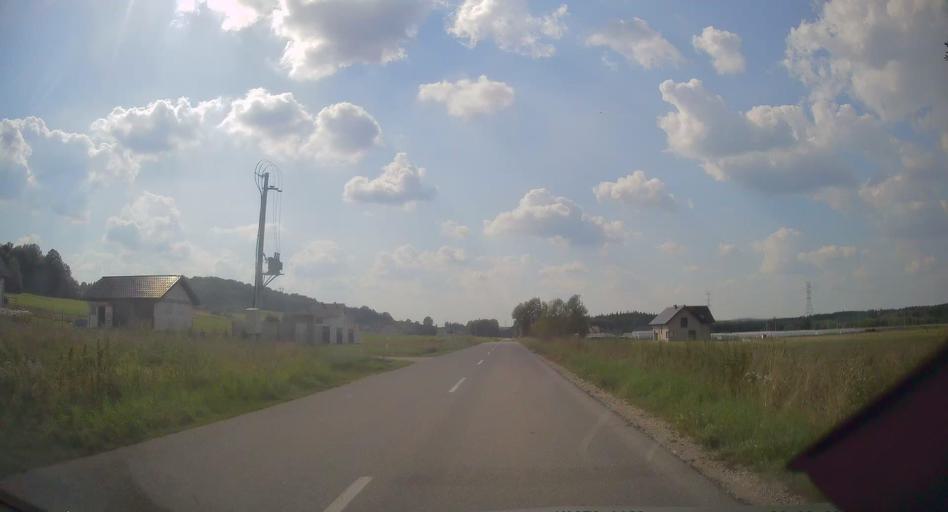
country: PL
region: Swietokrzyskie
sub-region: Powiat jedrzejowski
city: Malogoszcz
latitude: 50.8621
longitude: 20.3398
